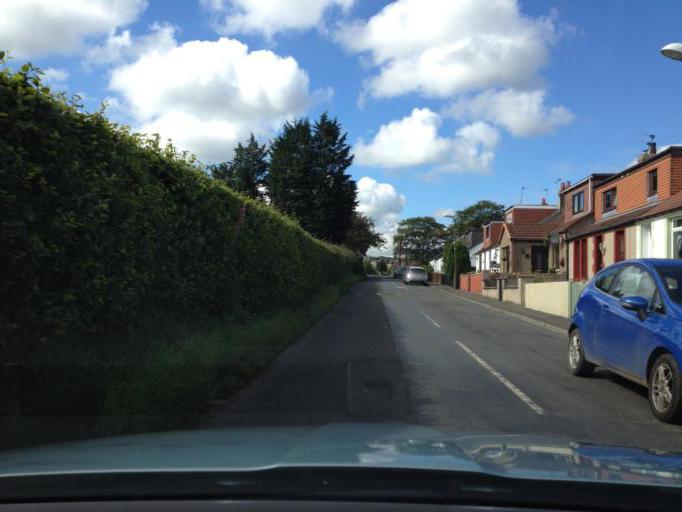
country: GB
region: Scotland
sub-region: West Lothian
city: Armadale
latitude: 55.9205
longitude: -3.7026
